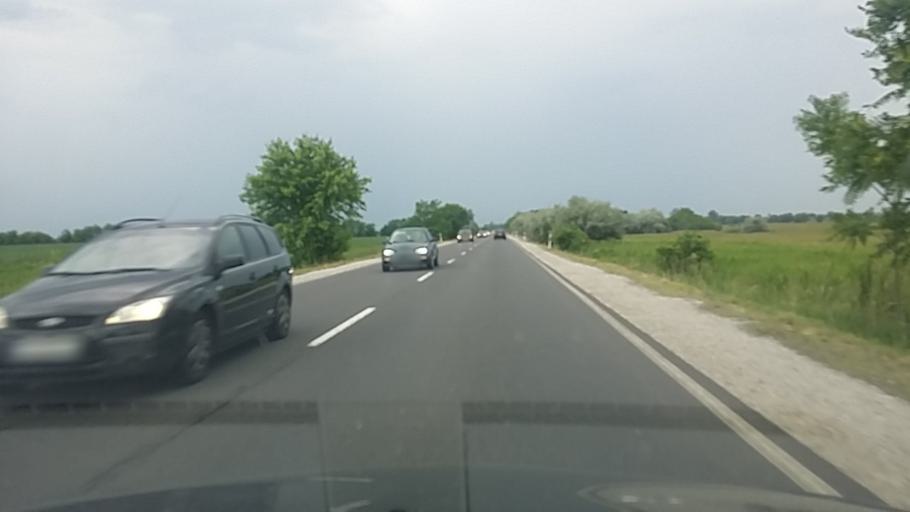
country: HU
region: Szabolcs-Szatmar-Bereg
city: Ujfeherto
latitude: 47.7892
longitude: 21.6943
